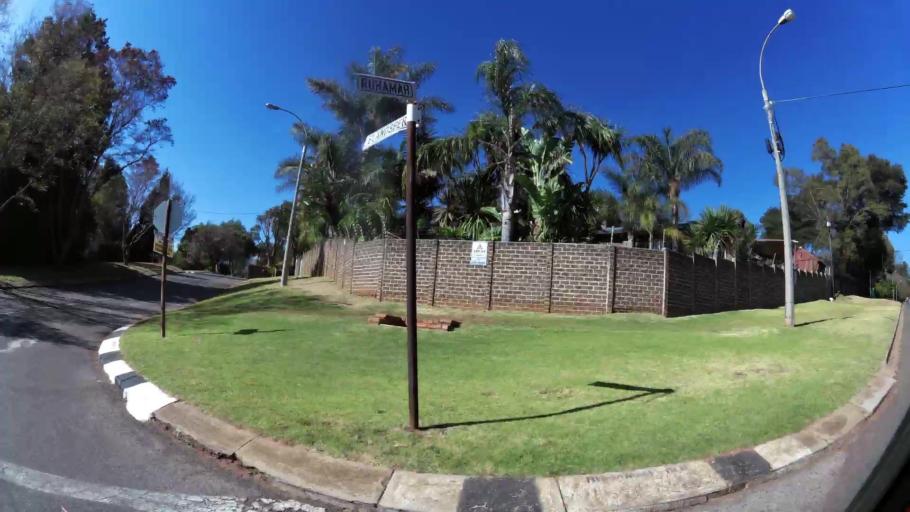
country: ZA
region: Gauteng
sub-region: City of Johannesburg Metropolitan Municipality
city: Roodepoort
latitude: -26.1203
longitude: 27.8681
